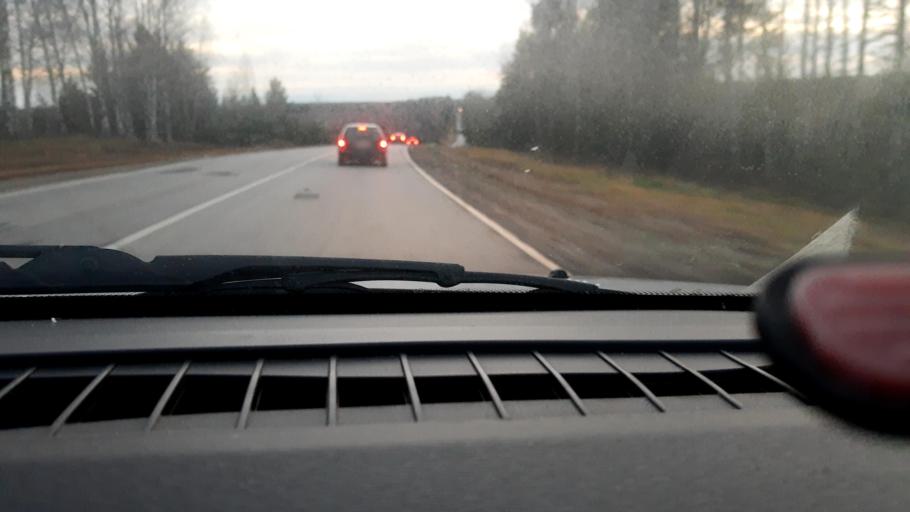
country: RU
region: Nizjnij Novgorod
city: Krasnyye Baki
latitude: 57.0472
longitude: 45.1346
